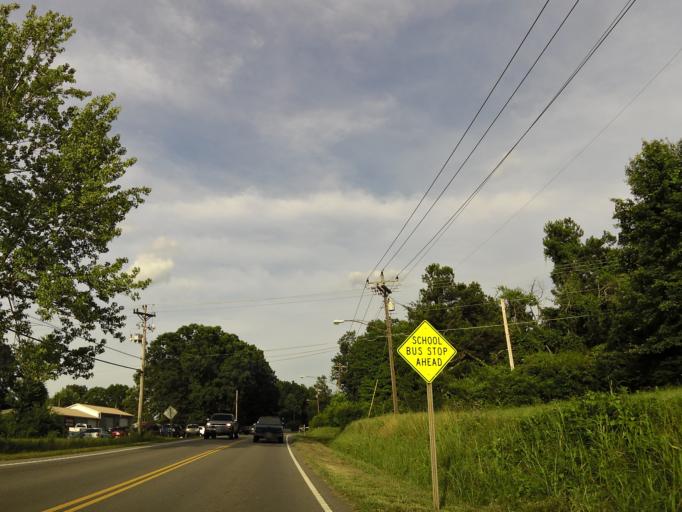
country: US
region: Tennessee
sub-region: Dickson County
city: Dickson
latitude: 36.0657
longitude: -87.3625
